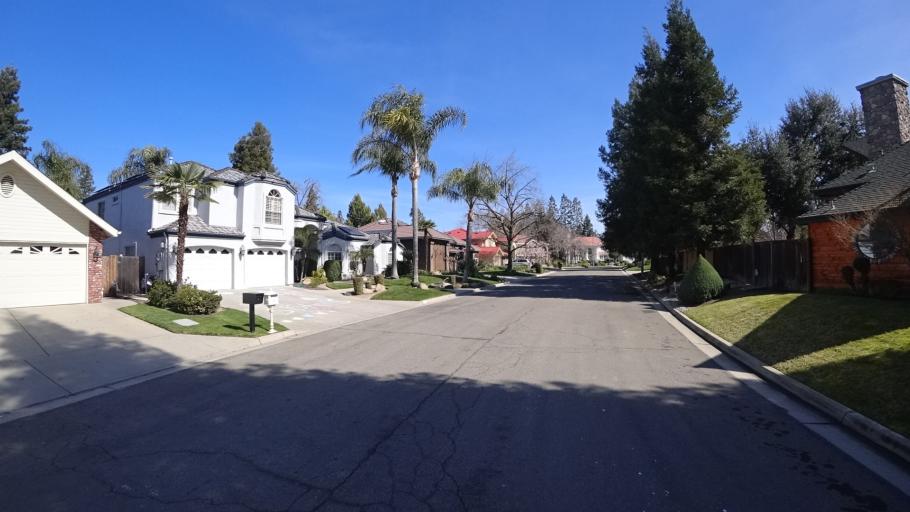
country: US
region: California
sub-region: Fresno County
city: Clovis
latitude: 36.8928
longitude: -119.7699
